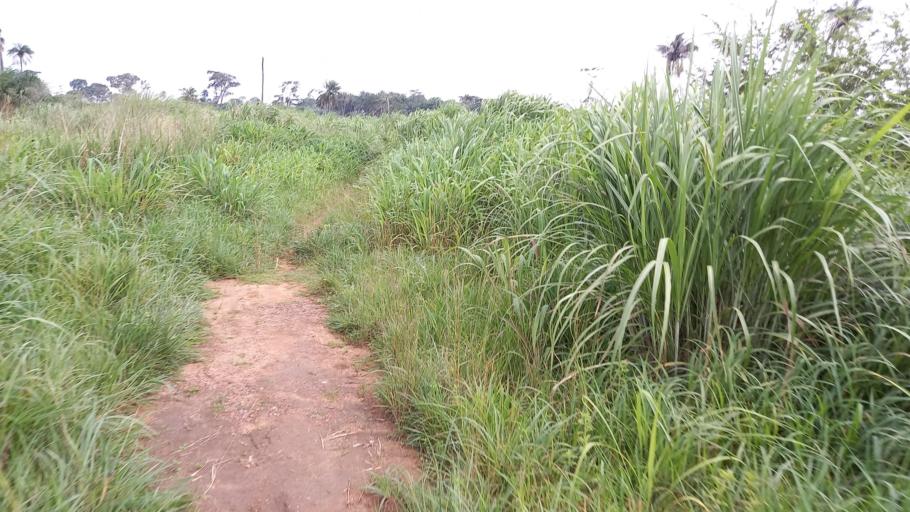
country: SL
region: Eastern Province
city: Kailahun
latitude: 8.2985
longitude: -10.5733
